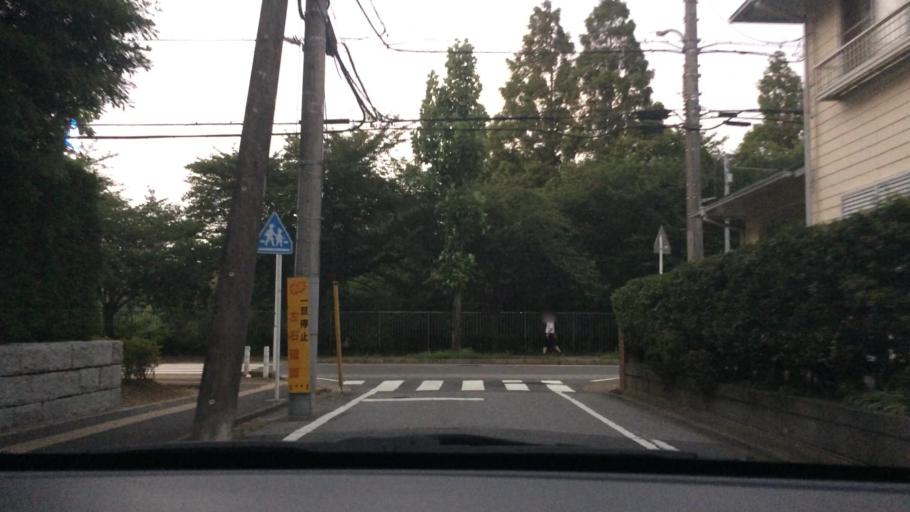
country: JP
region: Chiba
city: Nagareyama
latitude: 35.8927
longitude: 139.9360
